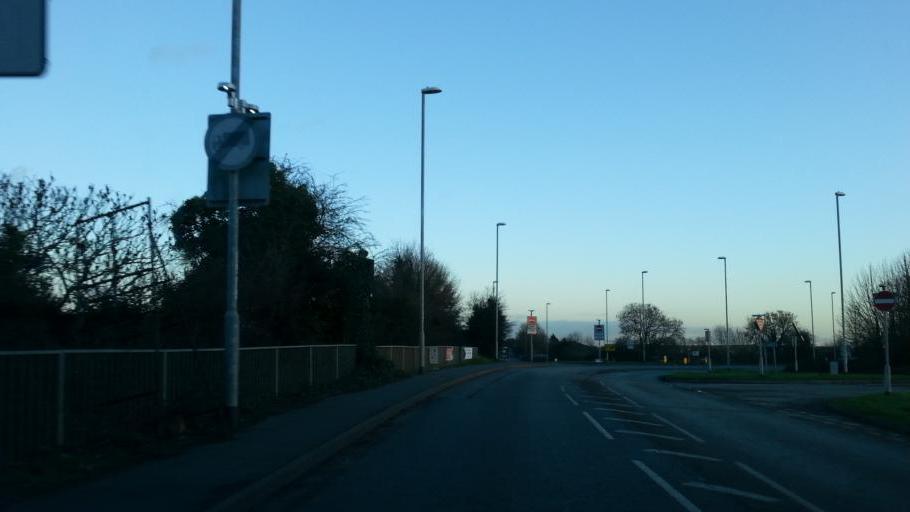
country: GB
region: England
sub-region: Cambridgeshire
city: Hemingford Grey
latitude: 52.2963
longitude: -0.0652
